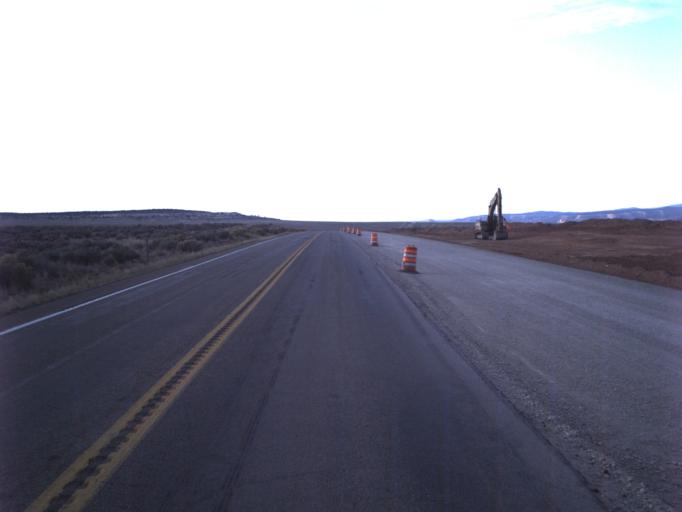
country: US
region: Utah
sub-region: San Juan County
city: Monticello
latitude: 38.1019
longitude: -109.3611
